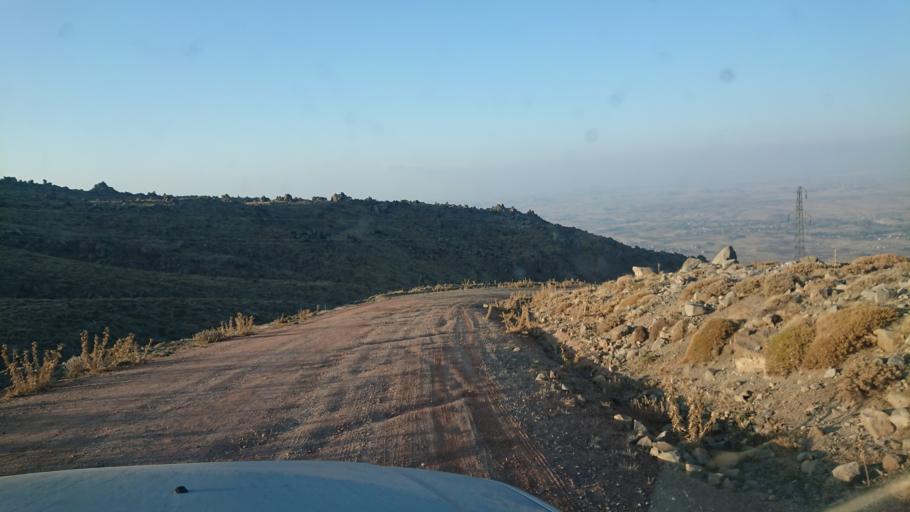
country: TR
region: Aksaray
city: Taspinar
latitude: 38.1601
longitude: 34.1714
